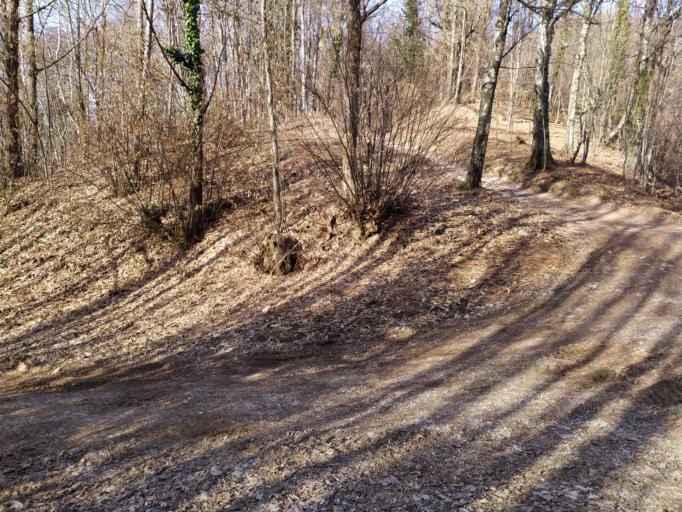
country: IT
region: Veneto
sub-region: Provincia di Vicenza
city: San Quirico
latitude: 45.7027
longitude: 11.2882
